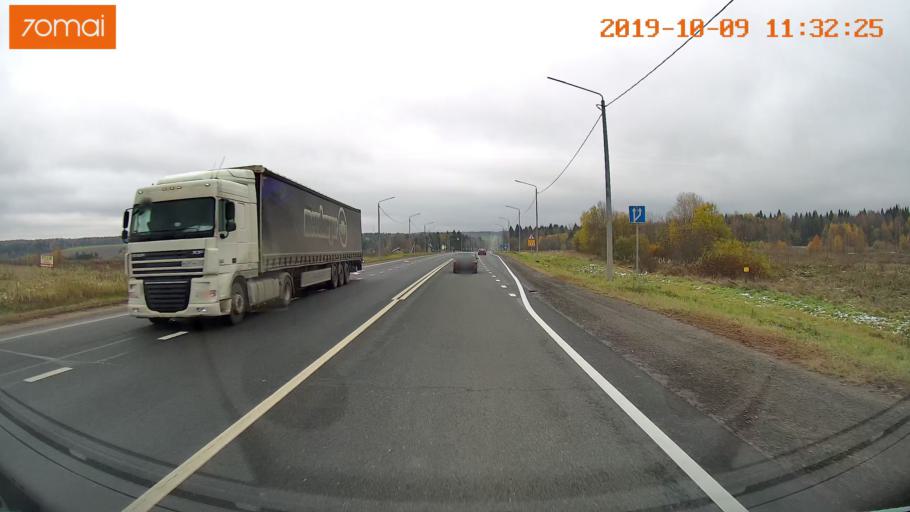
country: RU
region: Vologda
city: Gryazovets
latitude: 59.0360
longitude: 40.1081
